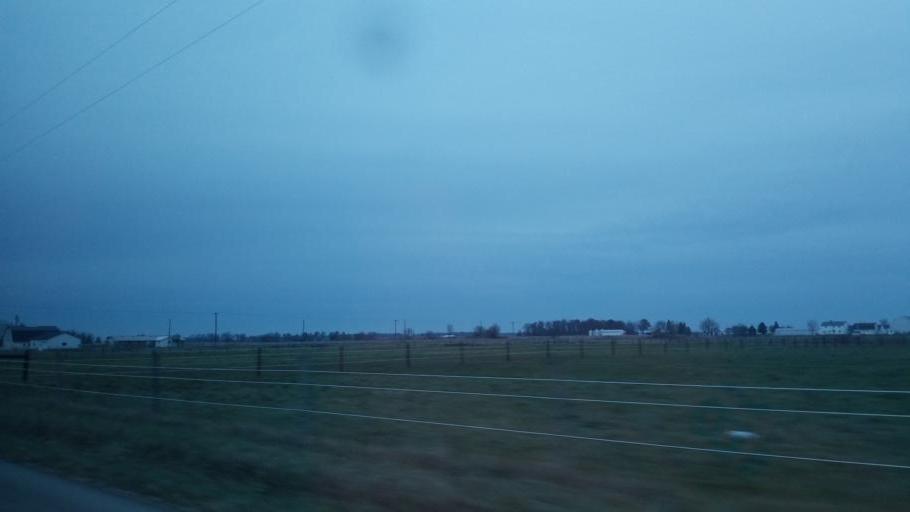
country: US
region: Indiana
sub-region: Adams County
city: Berne
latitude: 40.7295
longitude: -84.8984
